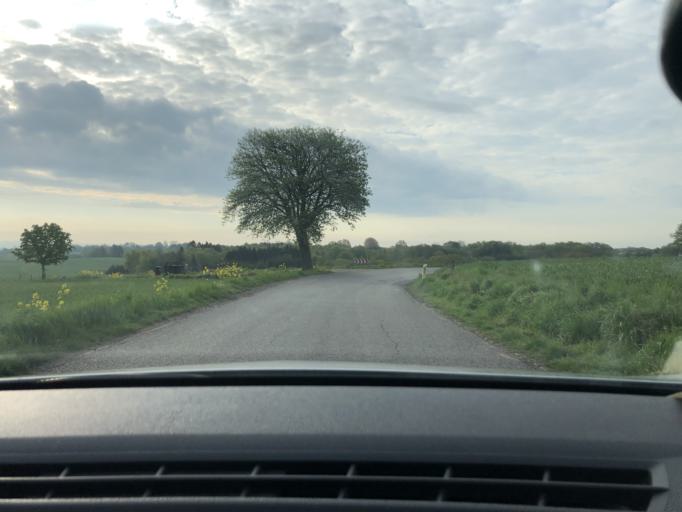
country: DK
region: Zealand
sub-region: Faxe Kommune
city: Ronnede
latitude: 55.2342
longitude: 12.0509
